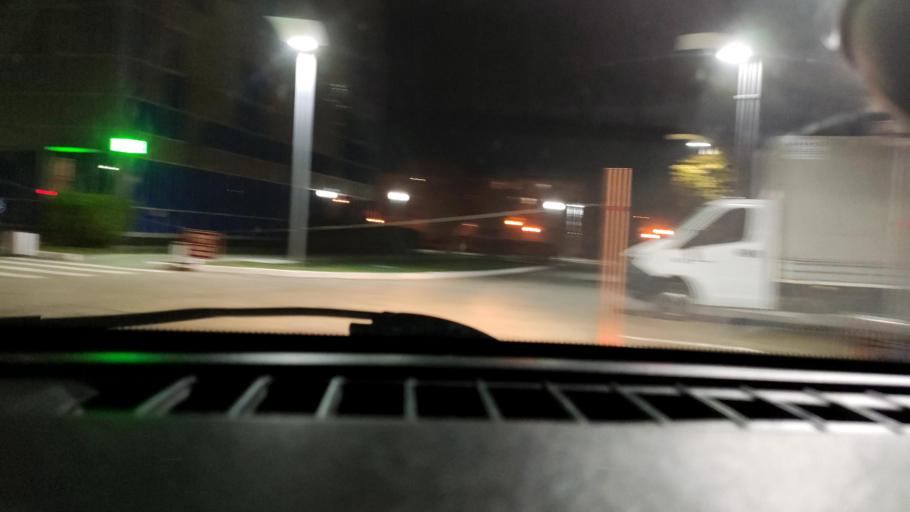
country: RU
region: Samara
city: Samara
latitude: 53.1898
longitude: 50.1785
